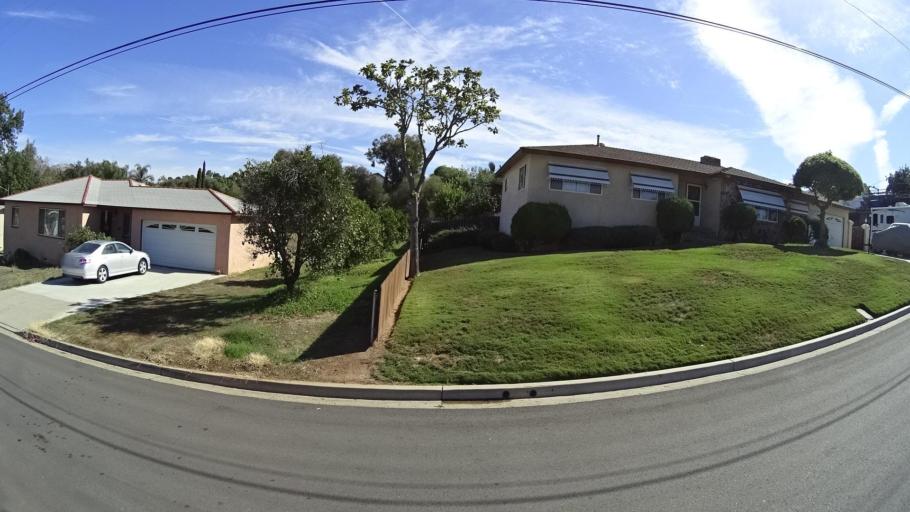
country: US
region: California
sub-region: San Diego County
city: Lakeside
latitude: 32.8420
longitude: -116.8997
